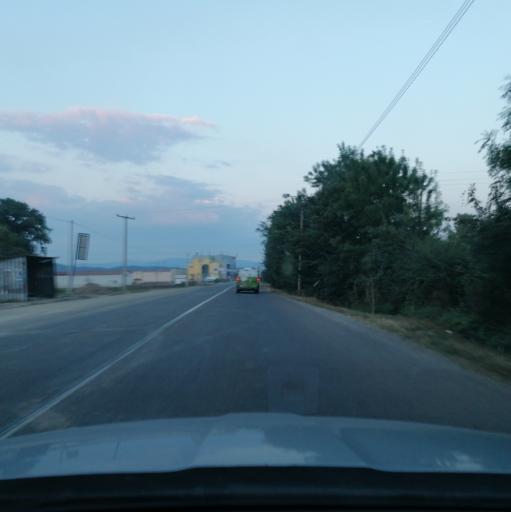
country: RS
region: Central Serbia
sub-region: Raski Okrug
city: Kraljevo
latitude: 43.7015
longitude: 20.7370
